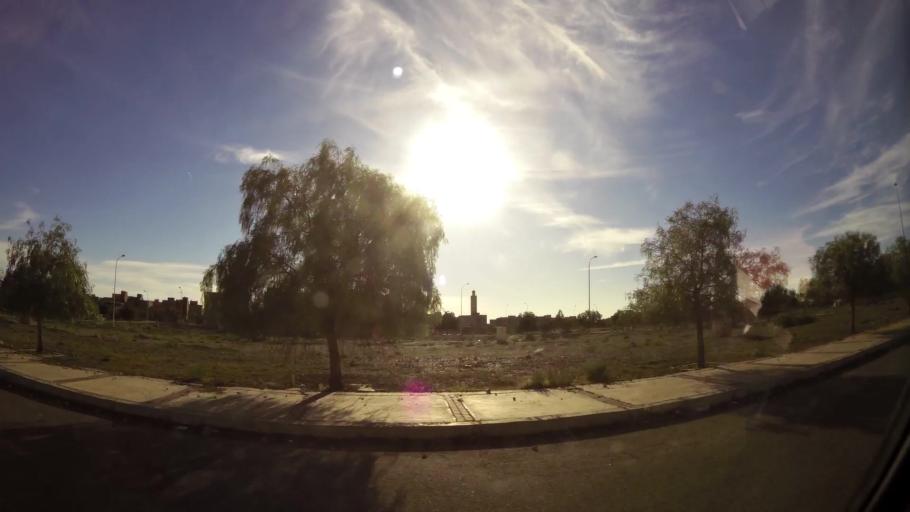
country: MA
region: Marrakech-Tensift-Al Haouz
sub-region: Marrakech
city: Marrakesh
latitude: 31.7578
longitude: -8.0946
